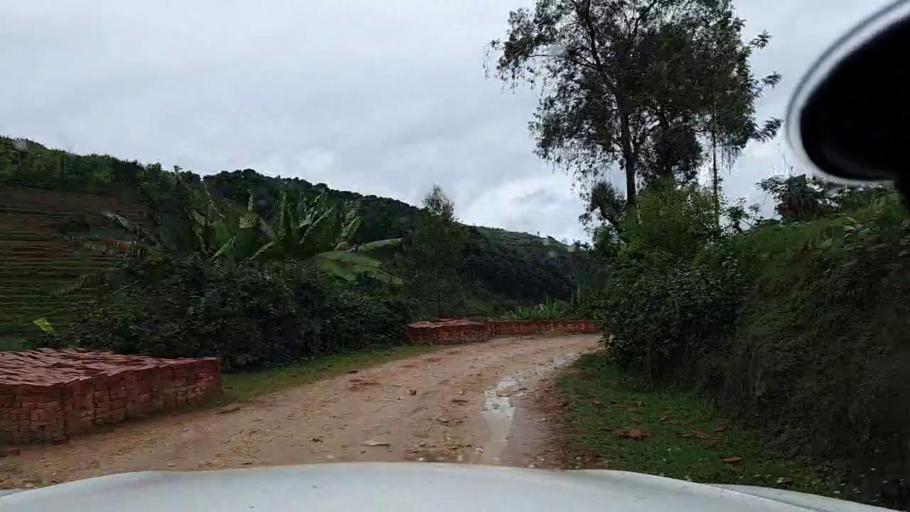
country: RW
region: Western Province
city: Kibuye
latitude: -2.1154
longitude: 29.4916
